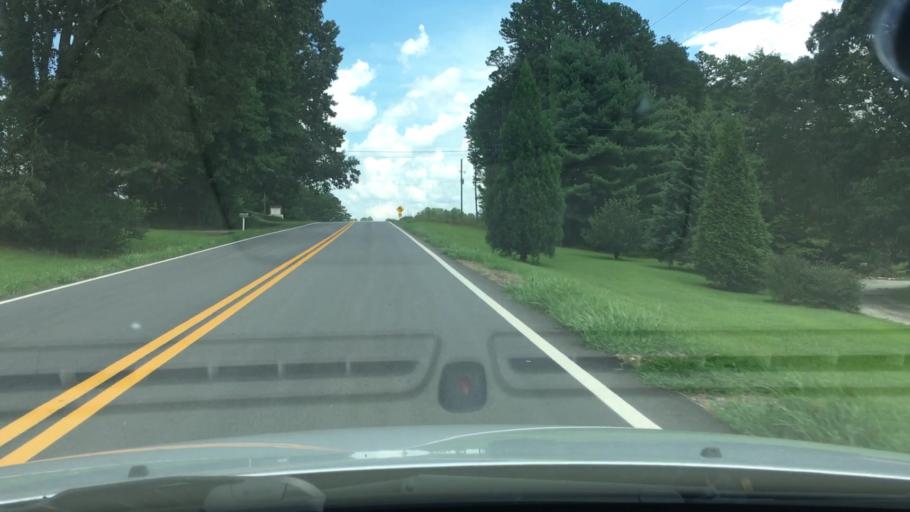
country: US
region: Georgia
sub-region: Lumpkin County
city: Dahlonega
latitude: 34.5591
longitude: -83.8912
